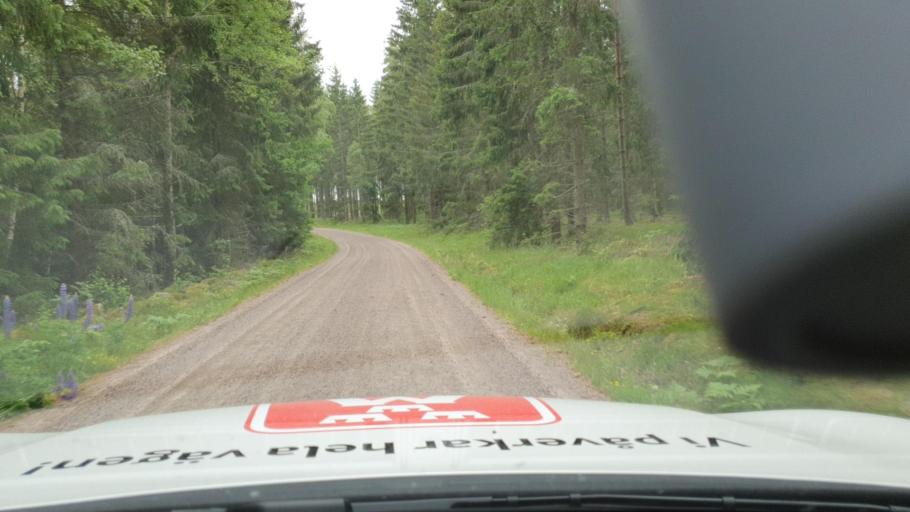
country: SE
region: Vaestra Goetaland
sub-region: Hjo Kommun
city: Hjo
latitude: 58.3962
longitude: 14.3400
